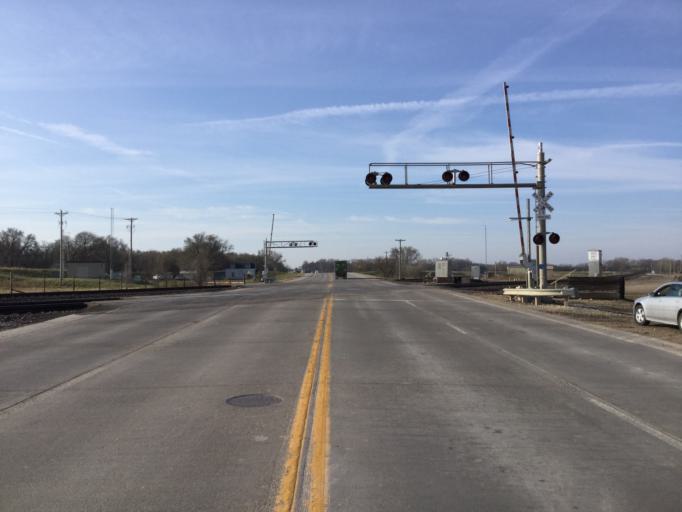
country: US
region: Kansas
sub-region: Butler County
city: Augusta
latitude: 37.6706
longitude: -96.9811
